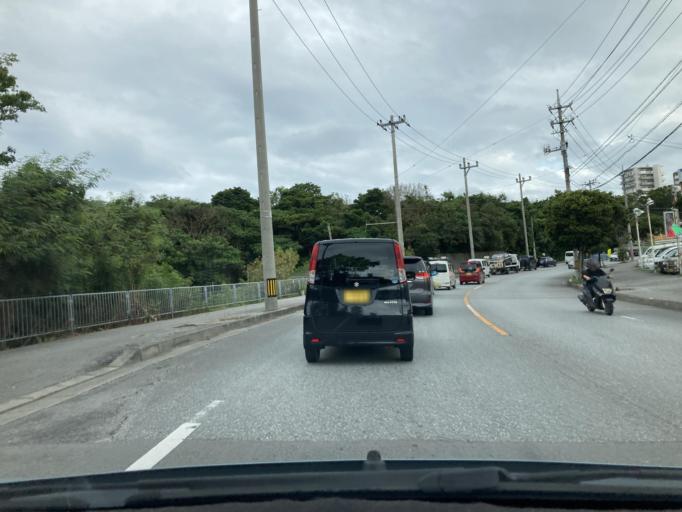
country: JP
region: Okinawa
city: Ginowan
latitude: 26.2452
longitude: 127.7640
